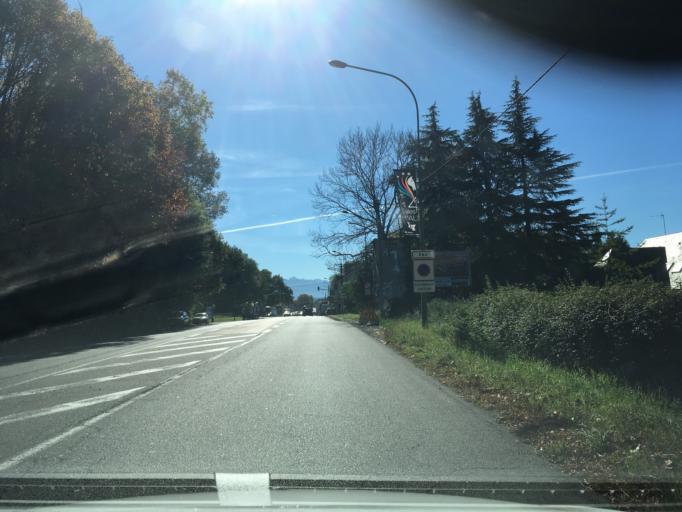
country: FR
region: Aquitaine
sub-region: Departement des Pyrenees-Atlantiques
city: Lons
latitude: 43.3370
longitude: -0.3798
